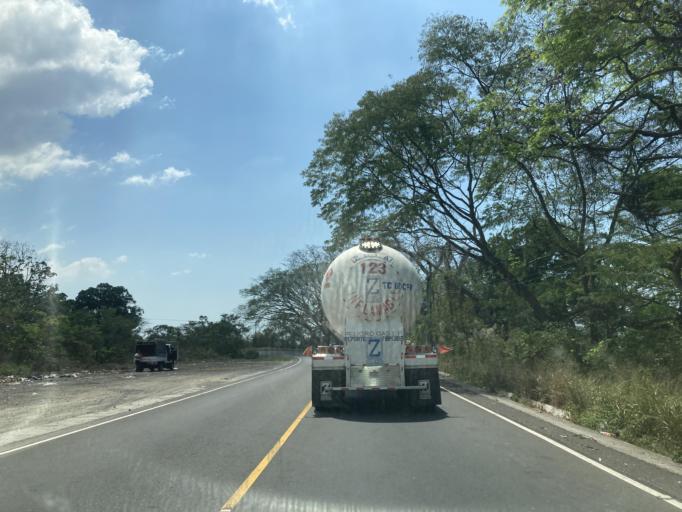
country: GT
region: Santa Rosa
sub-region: Municipio de Taxisco
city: Taxisco
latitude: 14.0988
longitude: -90.5321
